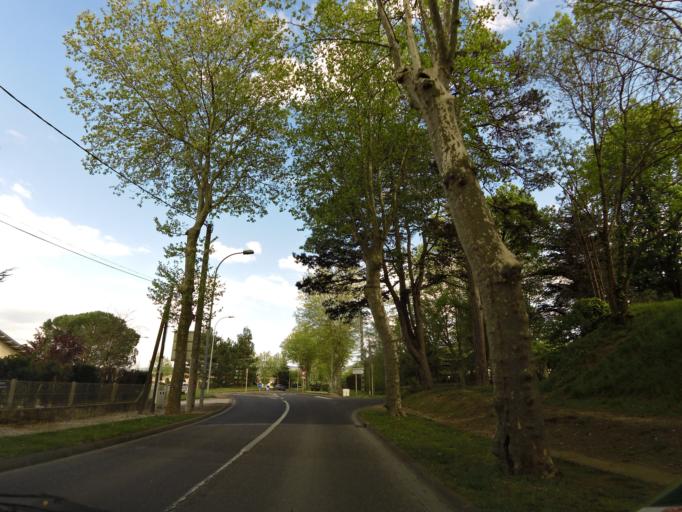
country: FR
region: Midi-Pyrenees
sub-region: Departement de la Haute-Garonne
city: Revel
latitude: 43.4555
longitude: 2.0142
